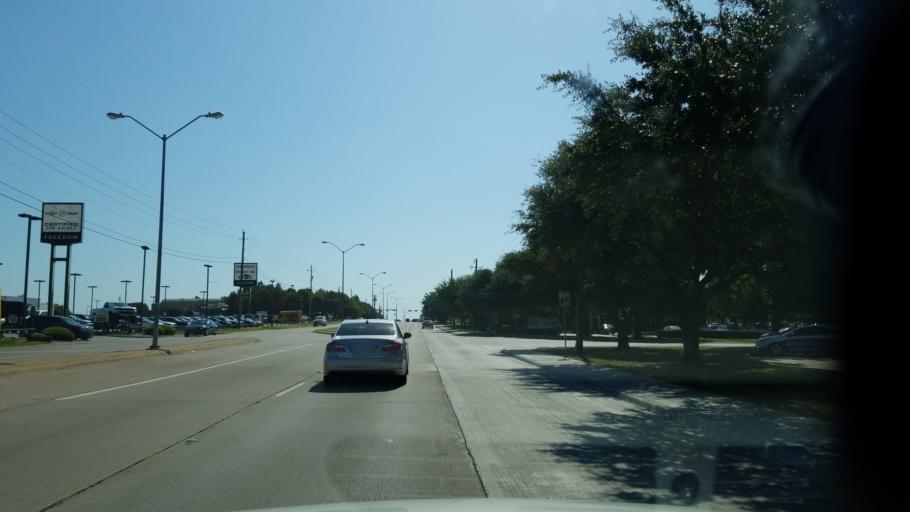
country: US
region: Texas
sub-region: Dallas County
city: Duncanville
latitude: 32.6474
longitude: -96.8825
